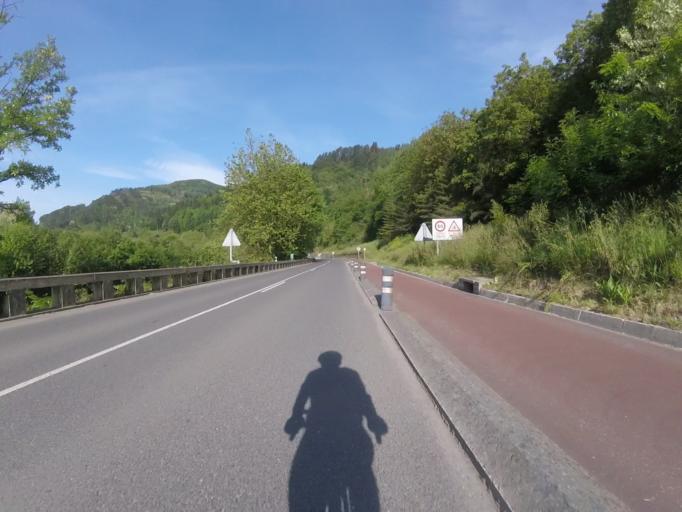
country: ES
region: Basque Country
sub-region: Provincia de Guipuzcoa
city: Legorreta
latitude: 43.0806
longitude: -2.1556
